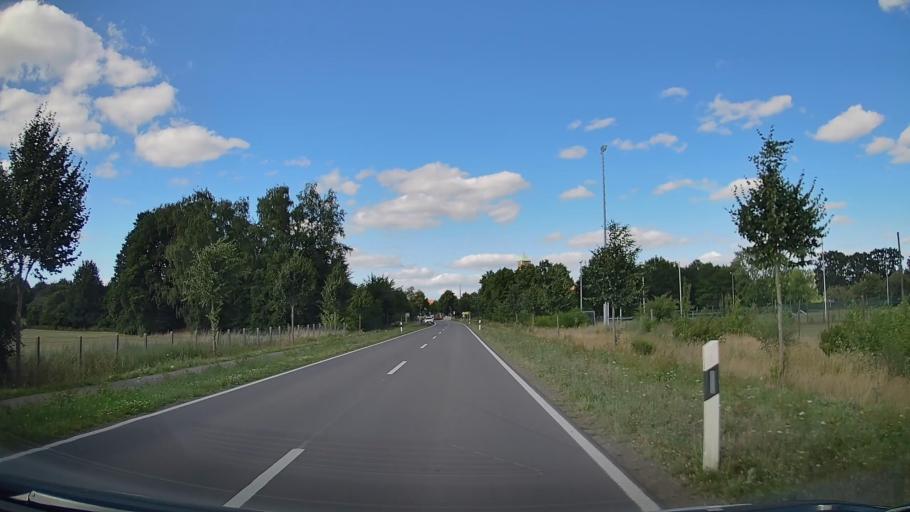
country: DE
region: Lower Saxony
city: Loningen
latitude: 52.7294
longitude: 7.7544
